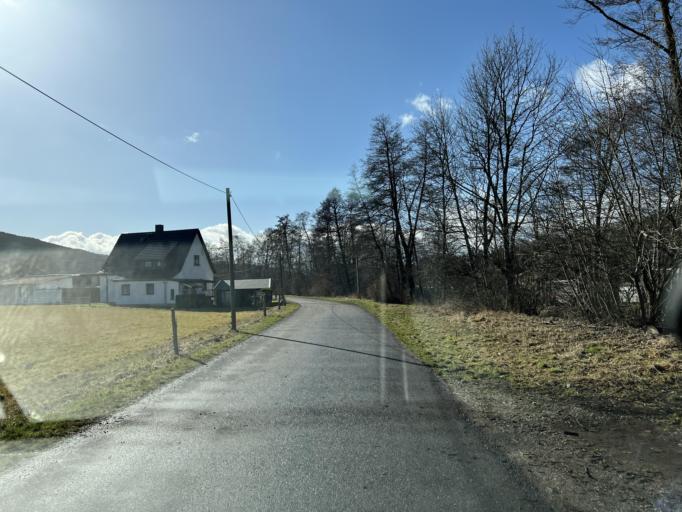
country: DE
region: Thuringia
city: Plaue
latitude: 50.7963
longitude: 10.9151
